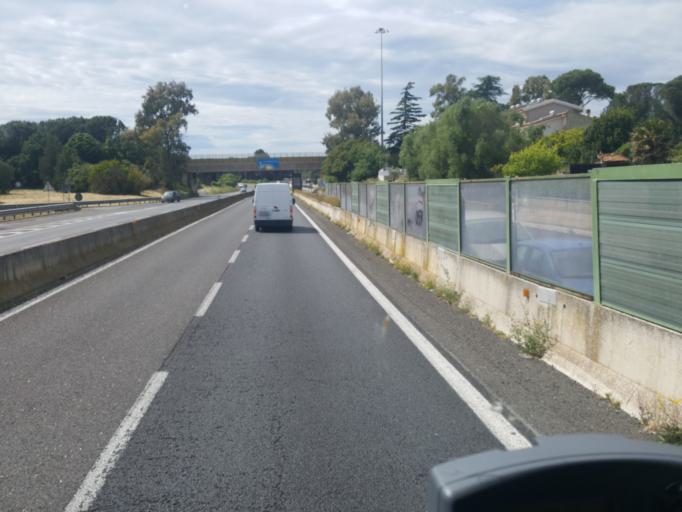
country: IT
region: Latium
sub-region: Citta metropolitana di Roma Capitale
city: Ara Nova
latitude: 41.9178
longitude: 12.2390
